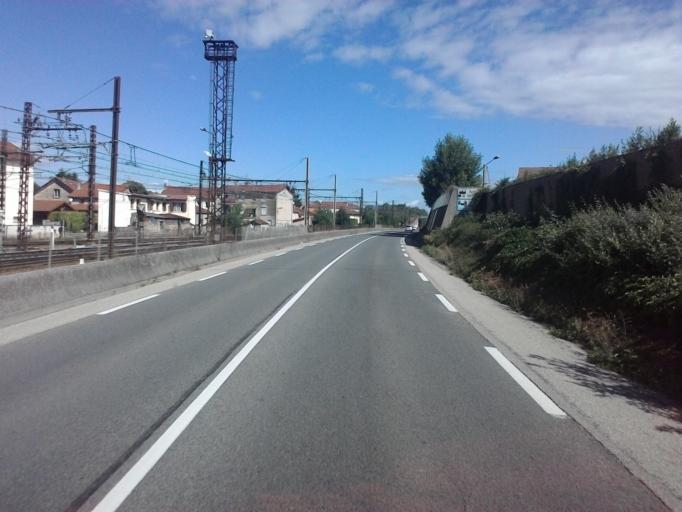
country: FR
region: Rhone-Alpes
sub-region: Departement de l'Ain
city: Amberieu-en-Bugey
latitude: 45.9568
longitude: 5.3515
